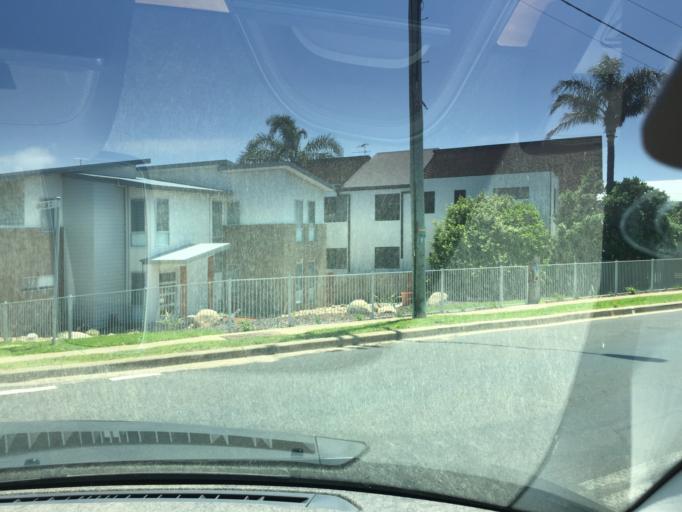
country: AU
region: New South Wales
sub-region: Bega Valley
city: Bega
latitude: -36.7325
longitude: 149.9817
